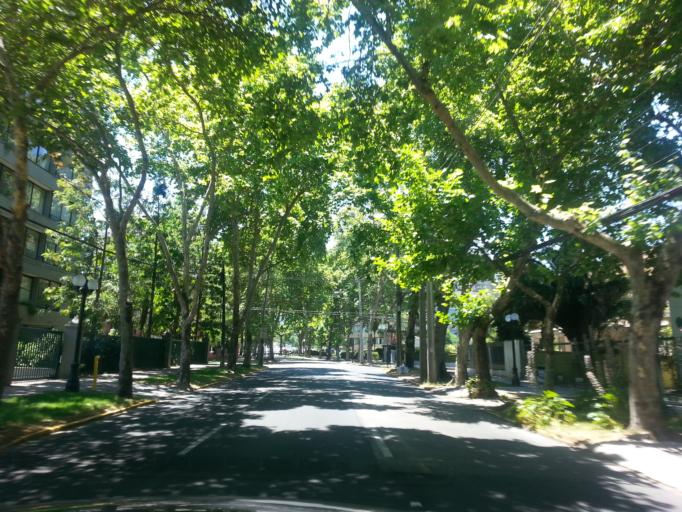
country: CL
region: Santiago Metropolitan
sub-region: Provincia de Santiago
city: Villa Presidente Frei, Nunoa, Santiago, Chile
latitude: -33.4252
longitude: -70.5948
